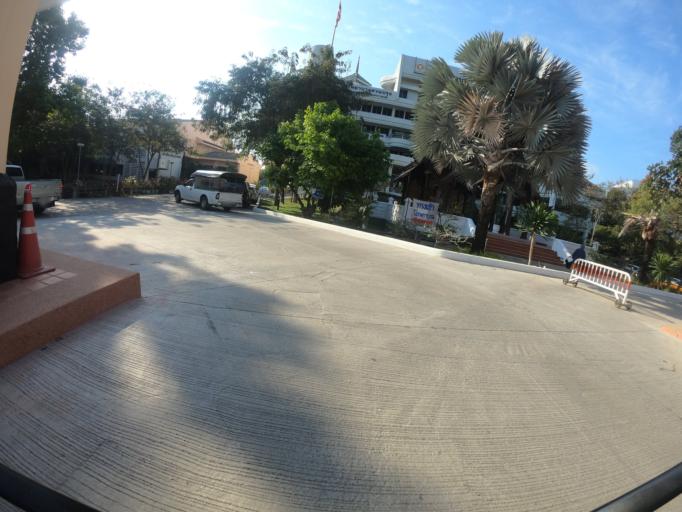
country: TH
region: Chiang Mai
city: Chiang Mai
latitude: 18.7811
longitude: 98.9793
